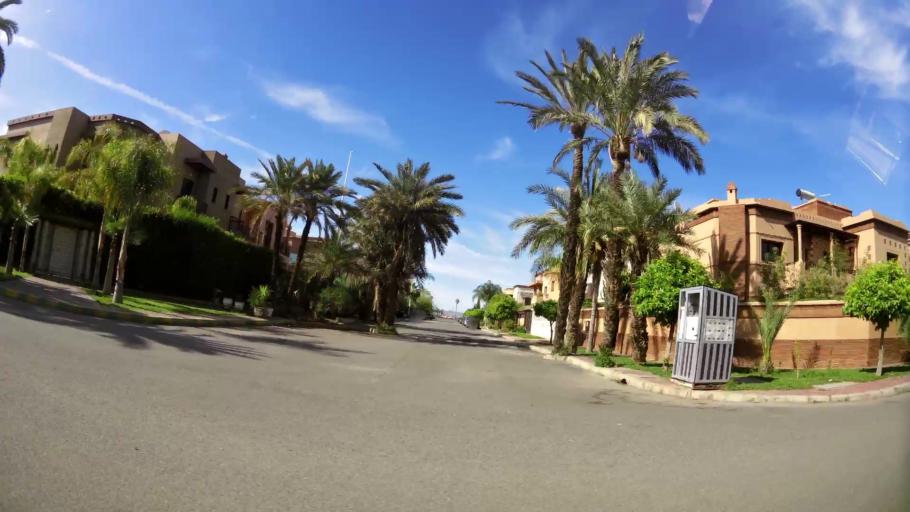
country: MA
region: Marrakech-Tensift-Al Haouz
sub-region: Marrakech
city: Marrakesh
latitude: 31.6513
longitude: -8.0441
